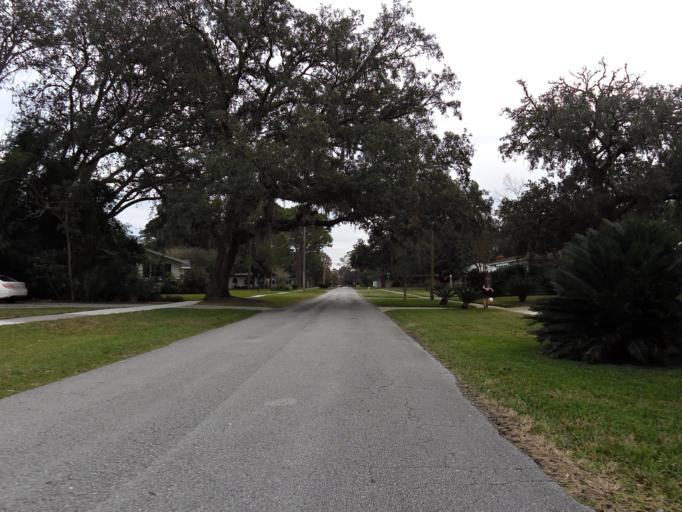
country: US
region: Florida
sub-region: Duval County
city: Jacksonville
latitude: 30.2460
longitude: -81.6278
